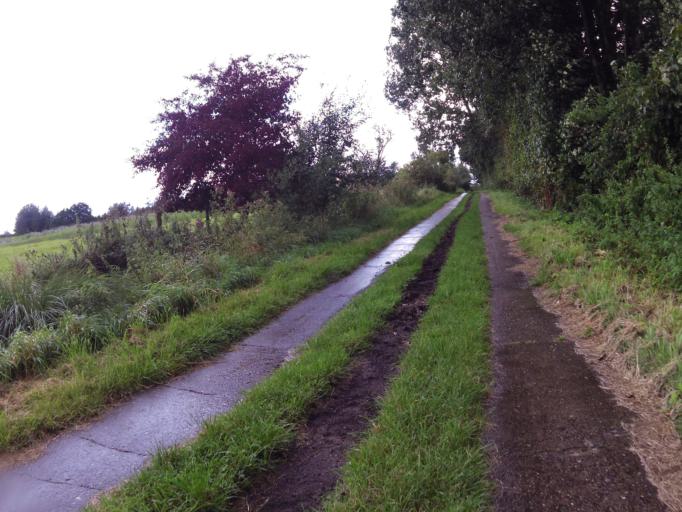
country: DE
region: Schleswig-Holstein
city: Krummbek
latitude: 54.4158
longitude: 10.3946
